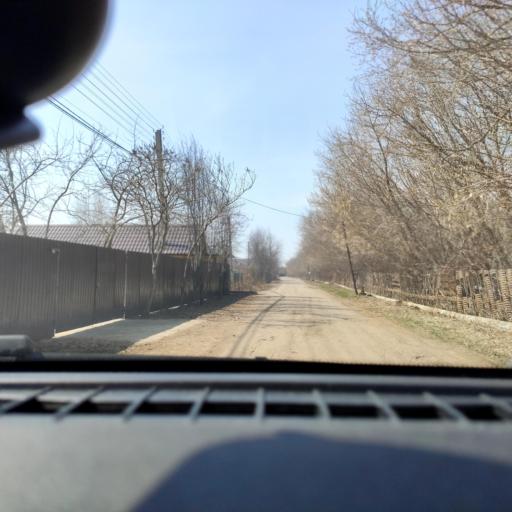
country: RU
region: Samara
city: Podstepki
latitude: 53.5206
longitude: 49.1036
